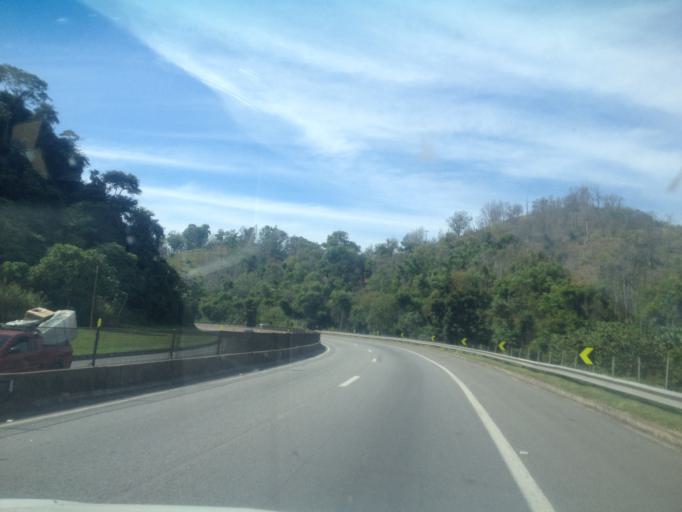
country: BR
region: Rio de Janeiro
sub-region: Pirai
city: Pirai
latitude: -22.6663
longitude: -43.8683
